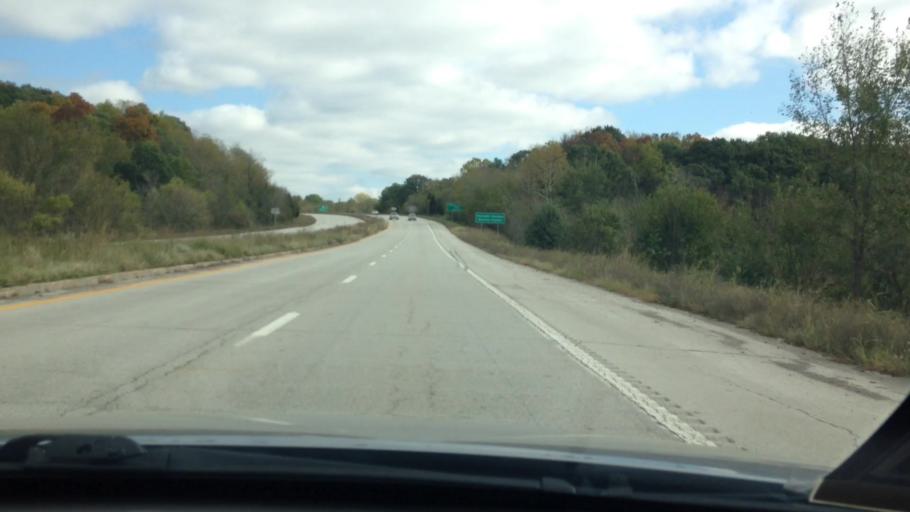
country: US
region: Missouri
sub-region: Platte County
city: Weatherby Lake
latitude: 39.2451
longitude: -94.7468
